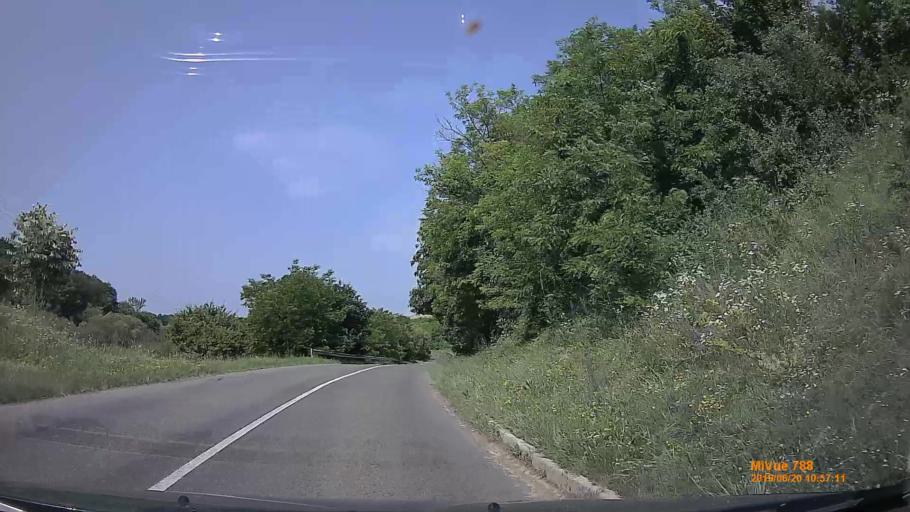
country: HU
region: Baranya
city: Mecseknadasd
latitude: 46.1534
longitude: 18.5245
